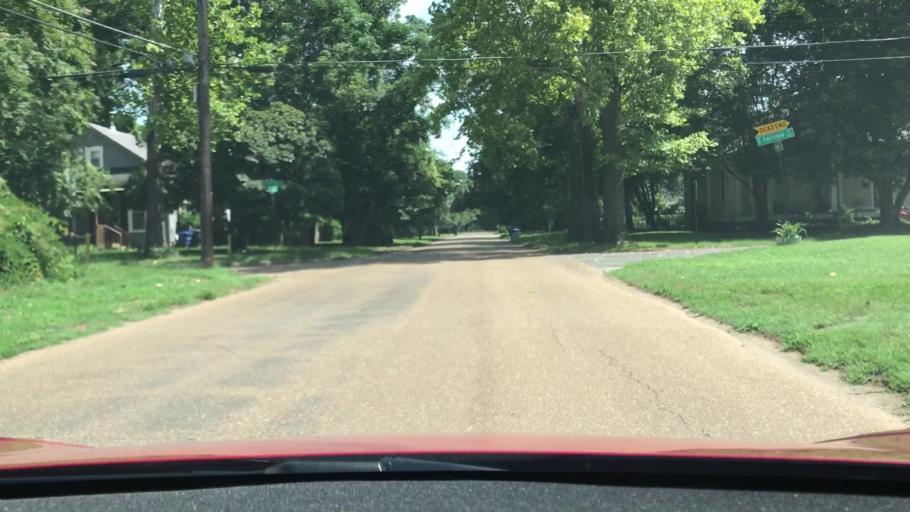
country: US
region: Louisiana
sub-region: Bossier Parish
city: Bossier City
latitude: 32.4766
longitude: -93.7312
